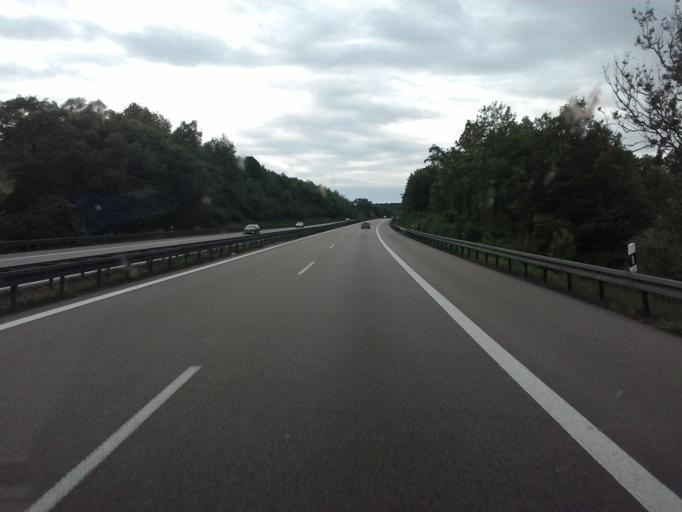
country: DE
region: Bavaria
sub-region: Upper Palatinate
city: Velburg
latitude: 49.2498
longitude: 11.6176
